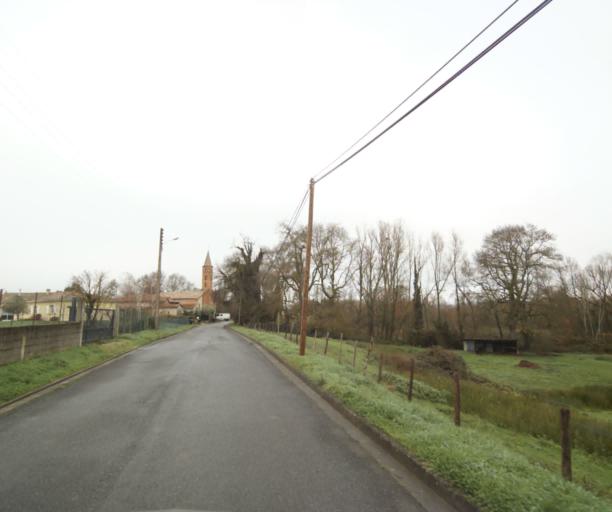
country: FR
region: Midi-Pyrenees
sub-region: Departement de la Haute-Garonne
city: Villemur-sur-Tarn
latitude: 43.8712
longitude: 1.4678
